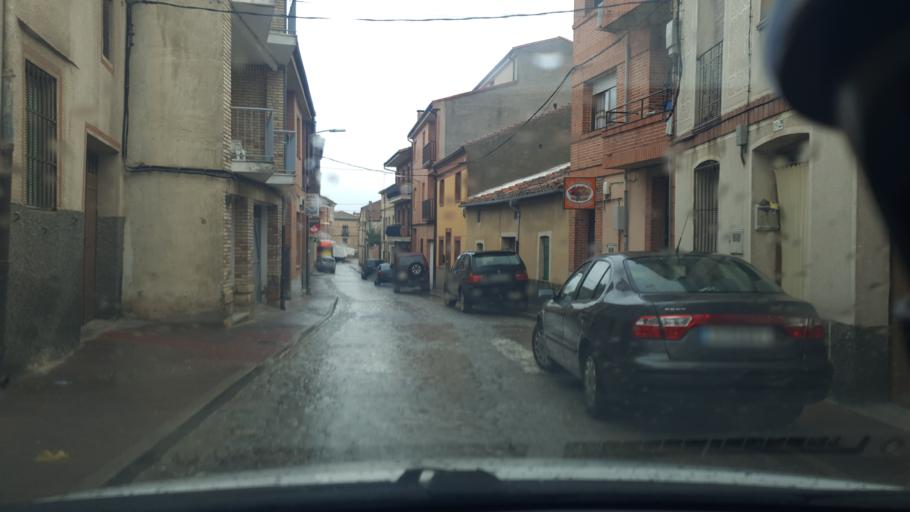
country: ES
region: Castille and Leon
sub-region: Provincia de Segovia
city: Carbonero el Mayor
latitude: 41.1212
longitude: -4.2650
